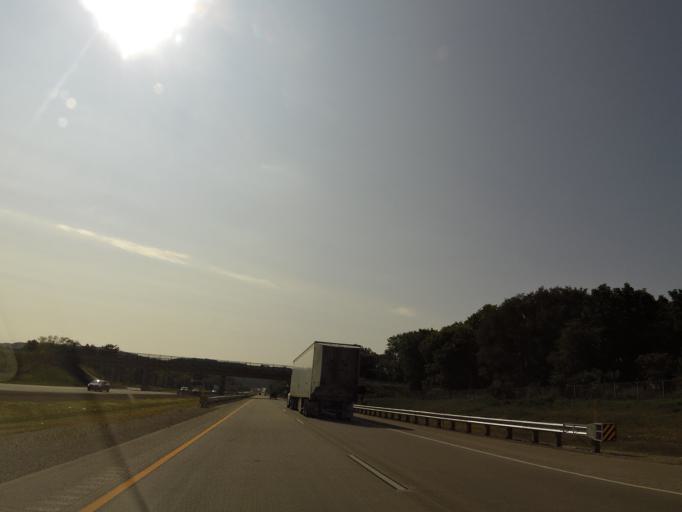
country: US
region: Wisconsin
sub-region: La Crosse County
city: French Island
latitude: 43.8606
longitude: -91.2679
